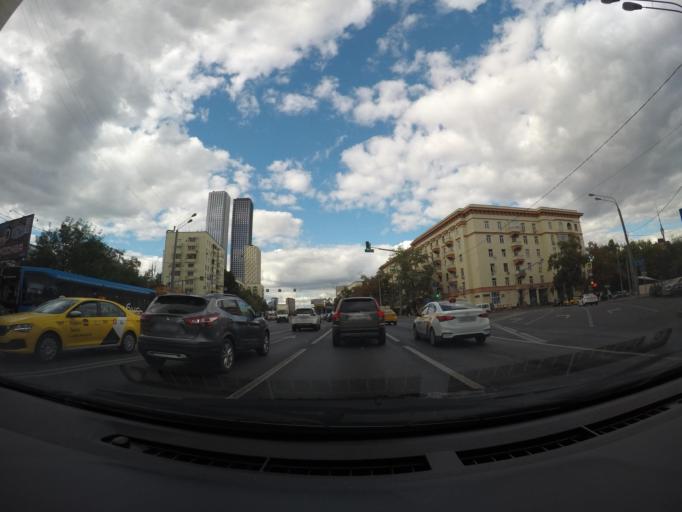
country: RU
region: Moscow
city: Mar'ina Roshcha
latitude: 55.8053
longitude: 37.5825
